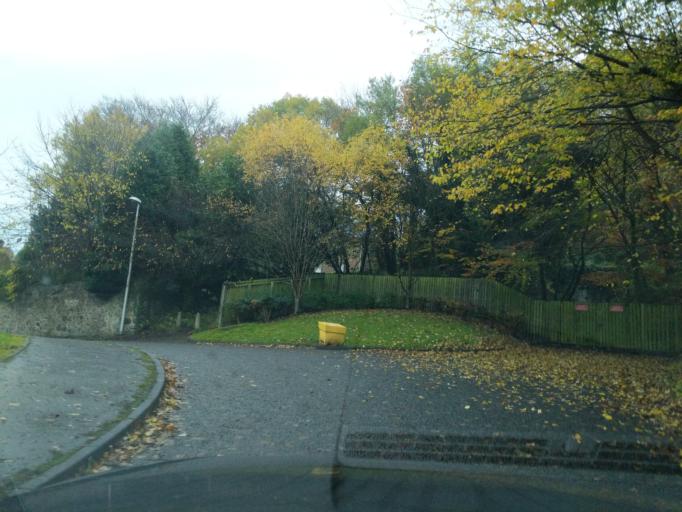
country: GB
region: Scotland
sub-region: Midlothian
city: Bonnyrigg
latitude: 55.8798
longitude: -3.1167
